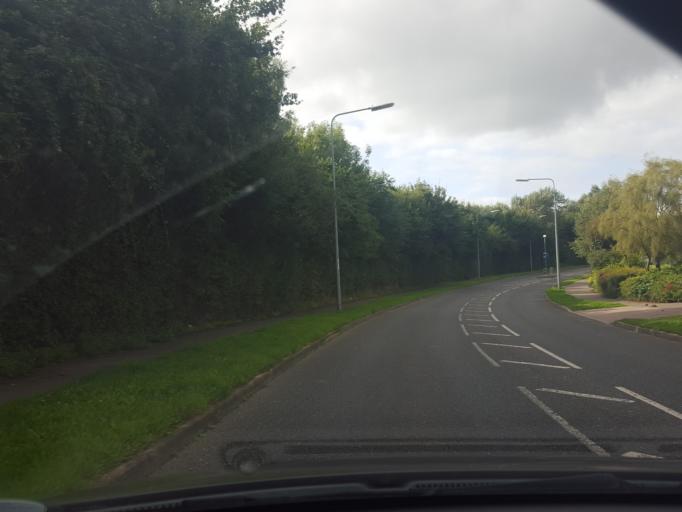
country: GB
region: England
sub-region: Essex
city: Dovercourt
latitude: 51.9245
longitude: 1.2480
